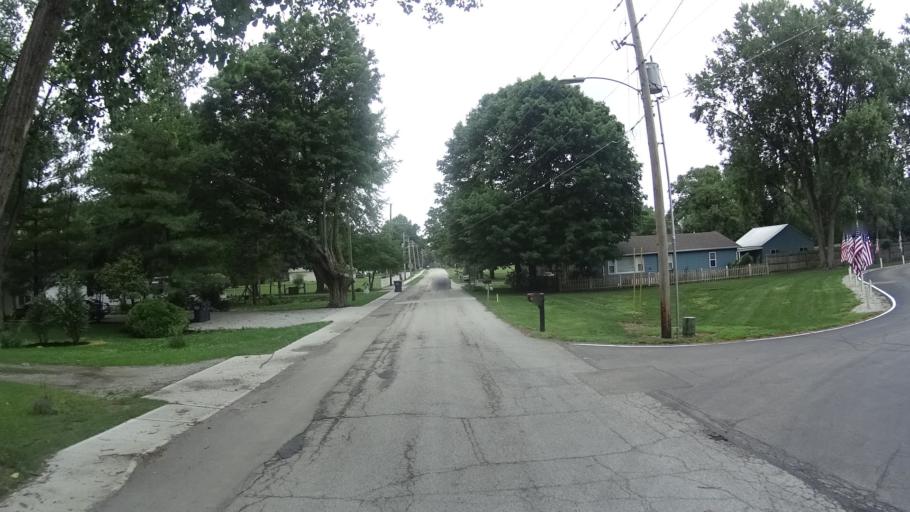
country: US
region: Indiana
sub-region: Madison County
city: Pendleton
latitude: 39.9893
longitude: -85.7443
